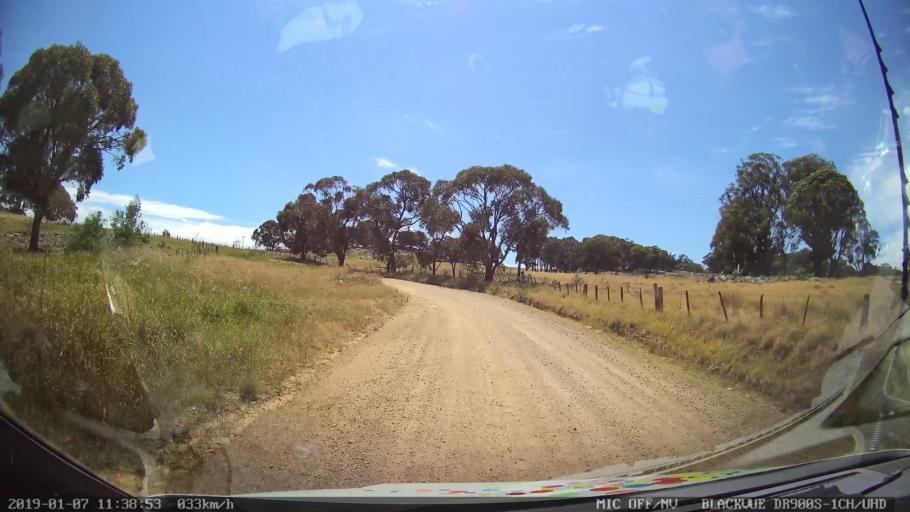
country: AU
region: New South Wales
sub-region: Armidale Dumaresq
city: Armidale
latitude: -30.3696
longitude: 151.5736
